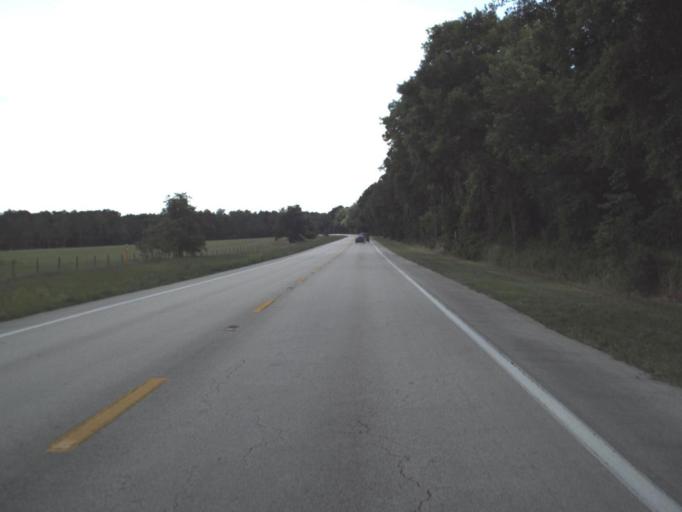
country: US
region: Florida
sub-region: Putnam County
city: Palatka
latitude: 29.5326
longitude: -81.6430
